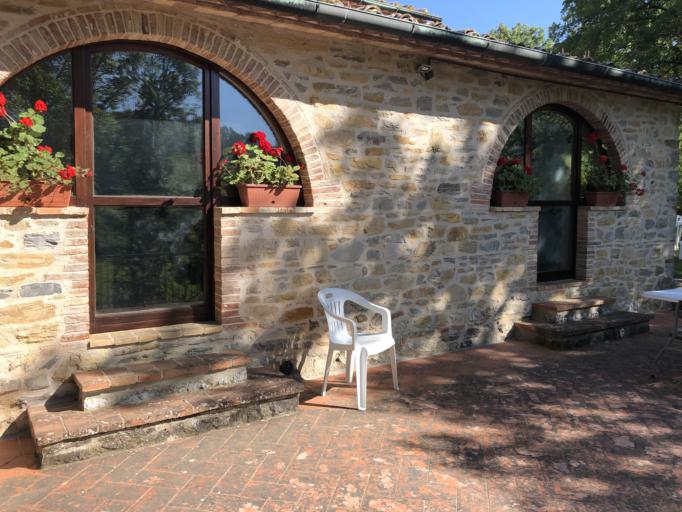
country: IT
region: Tuscany
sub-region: Province of Pisa
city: Castelnuovo di Val di Cecina
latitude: 43.2048
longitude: 10.9254
